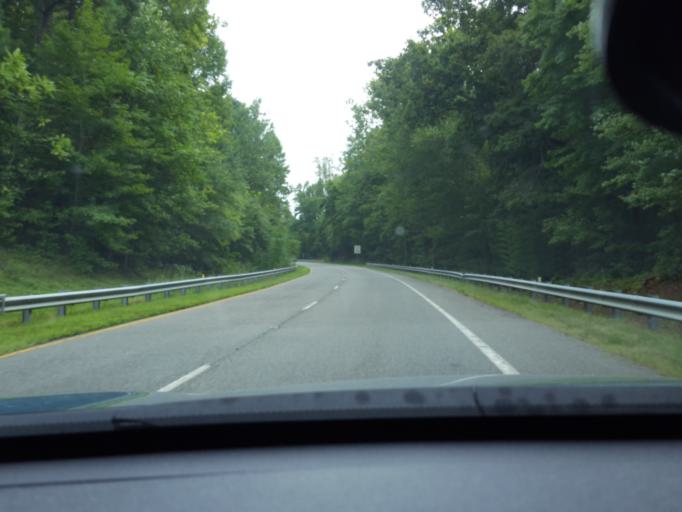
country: US
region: Virginia
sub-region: Caroline County
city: Bowling Green
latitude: 38.0563
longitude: -77.3432
